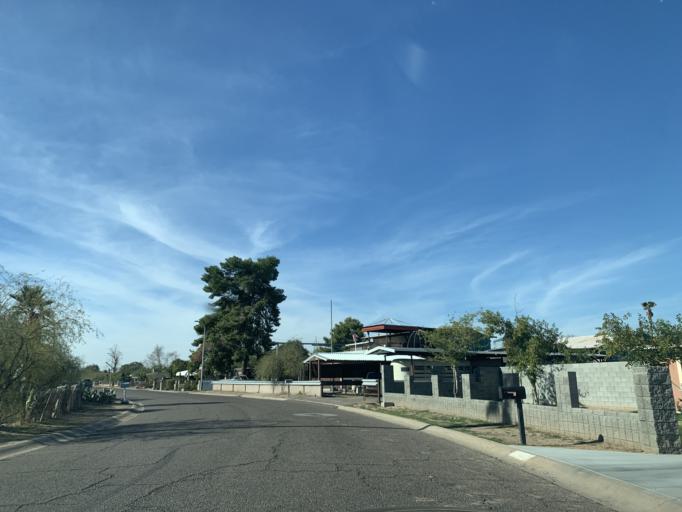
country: US
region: Arizona
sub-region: Maricopa County
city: Laveen
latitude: 33.3949
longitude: -112.1371
